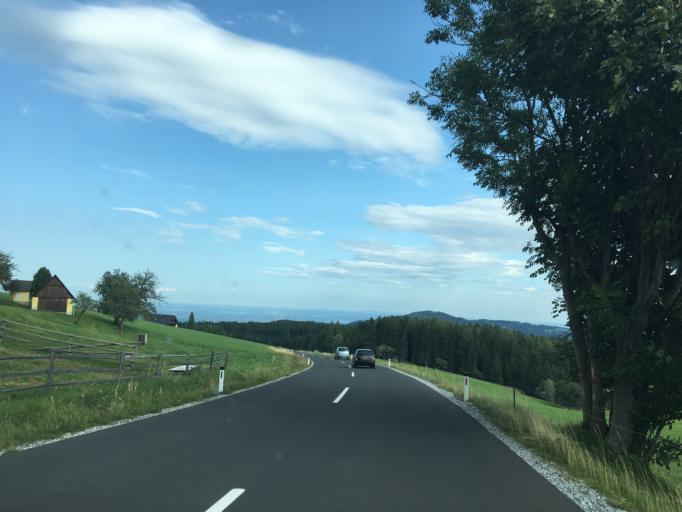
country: AT
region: Styria
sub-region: Politischer Bezirk Deutschlandsberg
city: Gressenberg
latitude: 46.8293
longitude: 15.0862
